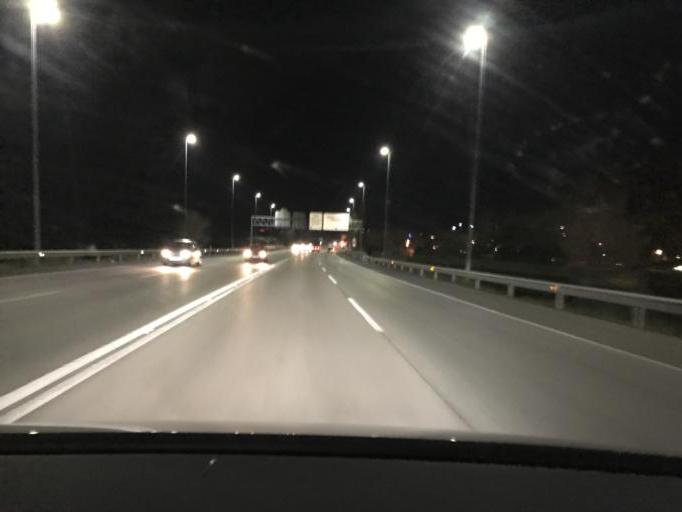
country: ES
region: Andalusia
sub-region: Provincia de Jaen
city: Jaen
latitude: 37.7894
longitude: -3.7757
